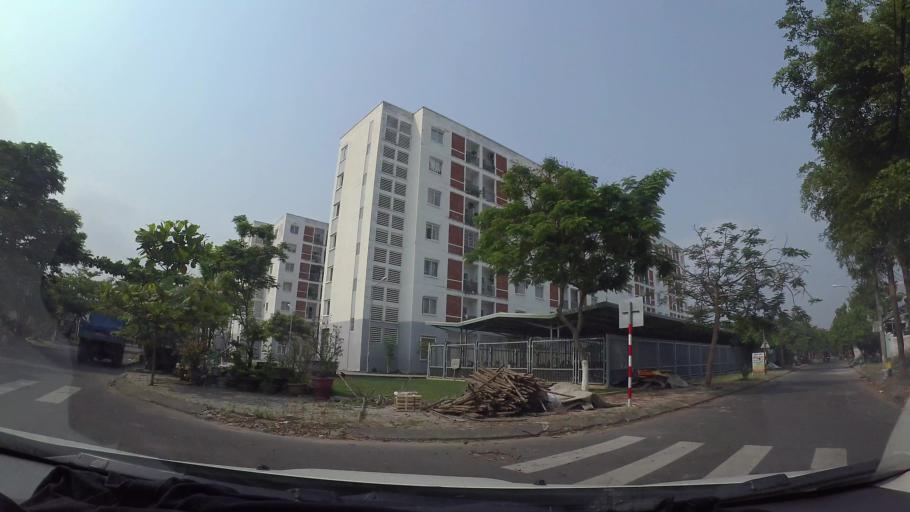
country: VN
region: Da Nang
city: Cam Le
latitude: 15.9994
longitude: 108.2149
